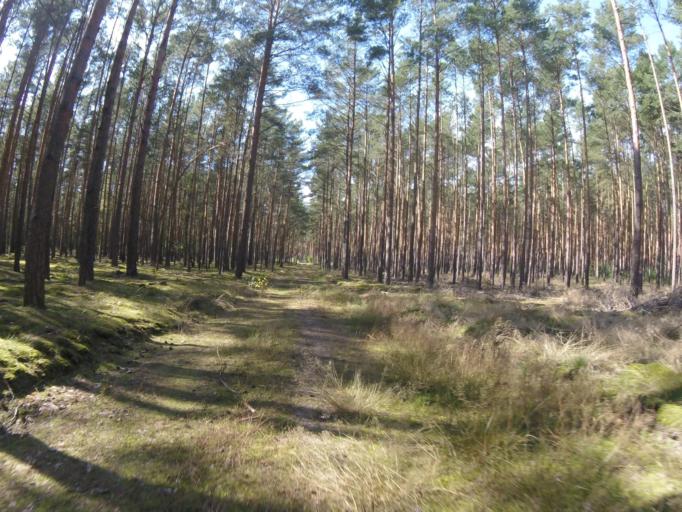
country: DE
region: Brandenburg
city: Bestensee
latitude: 52.2436
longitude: 13.6853
